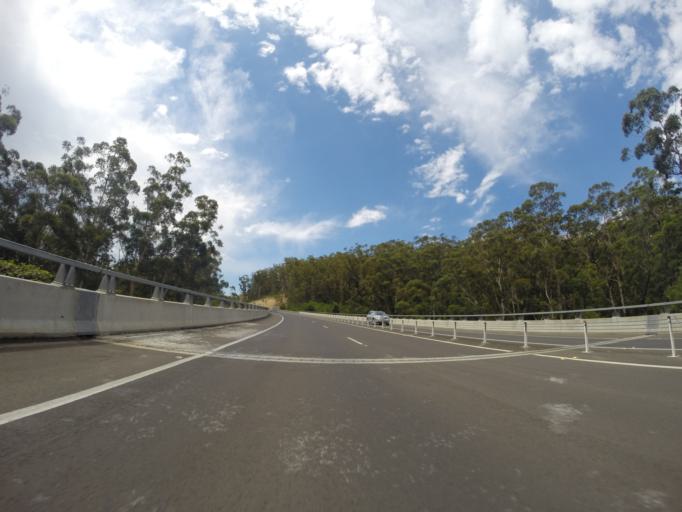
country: AU
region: New South Wales
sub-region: Shoalhaven Shire
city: Milton
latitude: -35.2079
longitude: 150.4387
